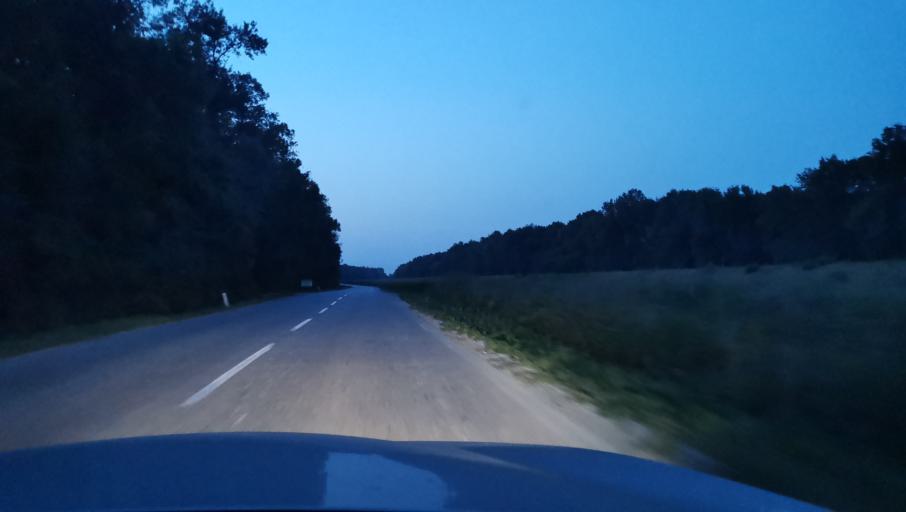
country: RS
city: Boljevci
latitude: 44.6990
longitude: 20.2015
